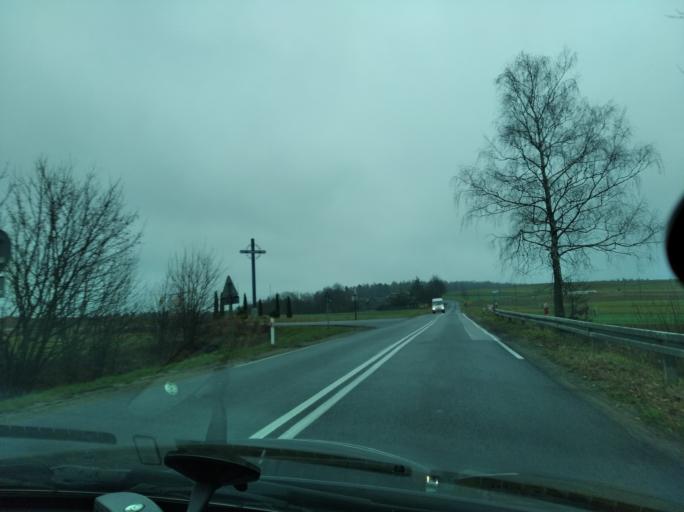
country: PL
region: Subcarpathian Voivodeship
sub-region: Powiat przeworski
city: Jawornik Polski
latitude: 49.8842
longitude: 22.2448
